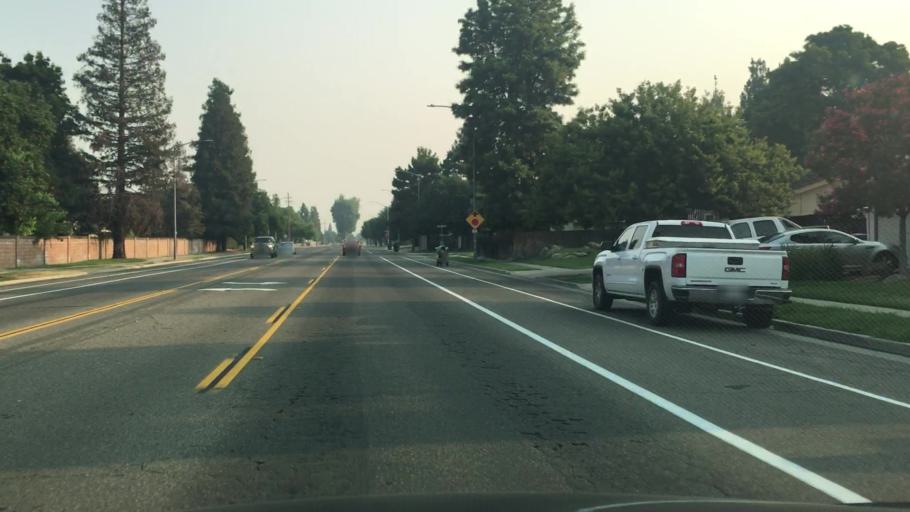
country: US
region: California
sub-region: Fresno County
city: Clovis
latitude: 36.8286
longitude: -119.6729
